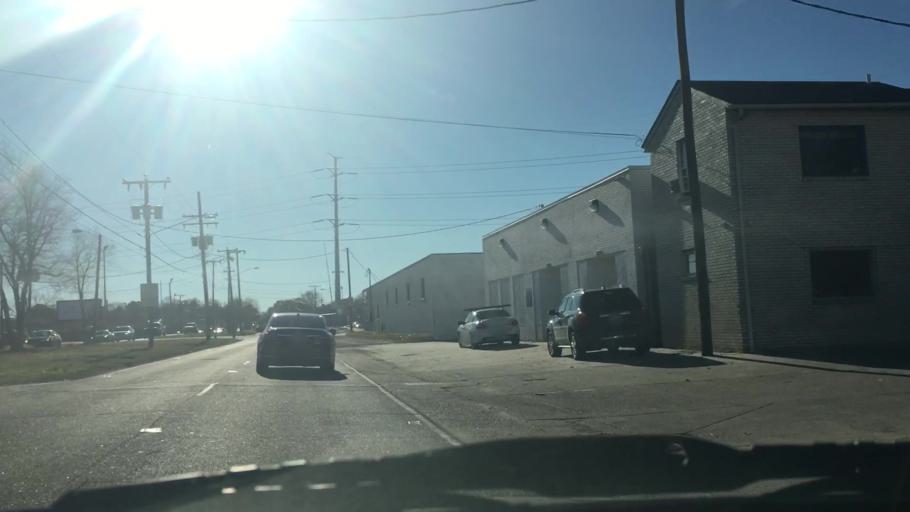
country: US
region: Virginia
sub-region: City of Norfolk
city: Norfolk
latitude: 36.8782
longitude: -76.2503
